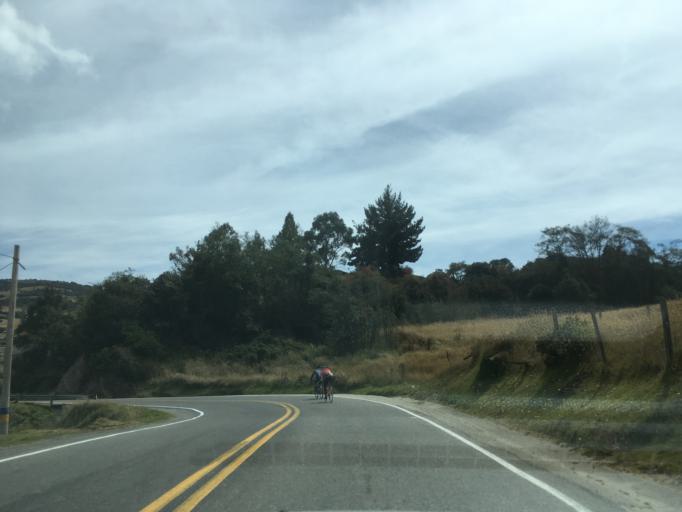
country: CO
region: Boyaca
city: Firavitoba
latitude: 5.6215
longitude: -72.9104
